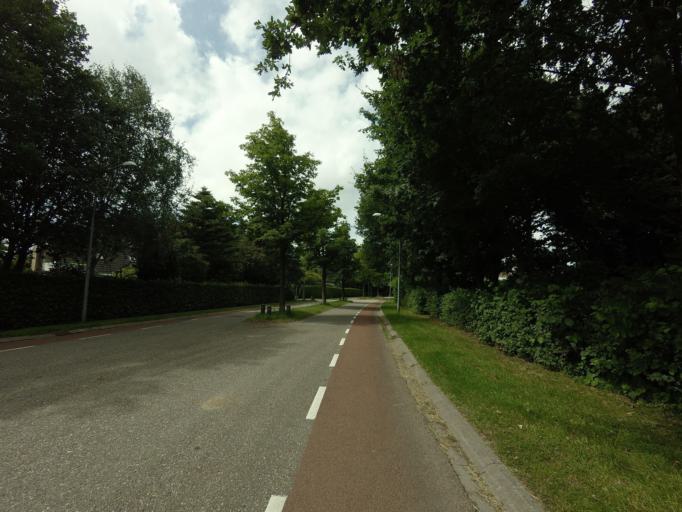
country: NL
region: North Holland
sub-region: Gemeente Huizen
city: Huizen
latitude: 52.3404
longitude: 5.3012
